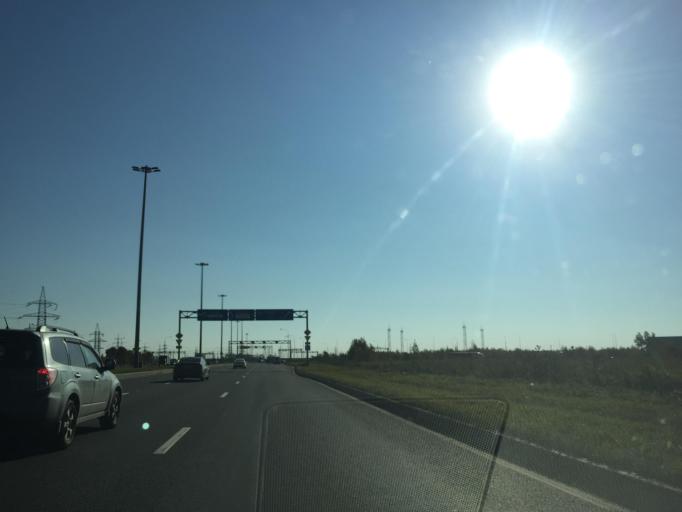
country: RU
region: St.-Petersburg
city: Metallostroy
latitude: 59.7511
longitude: 30.5270
